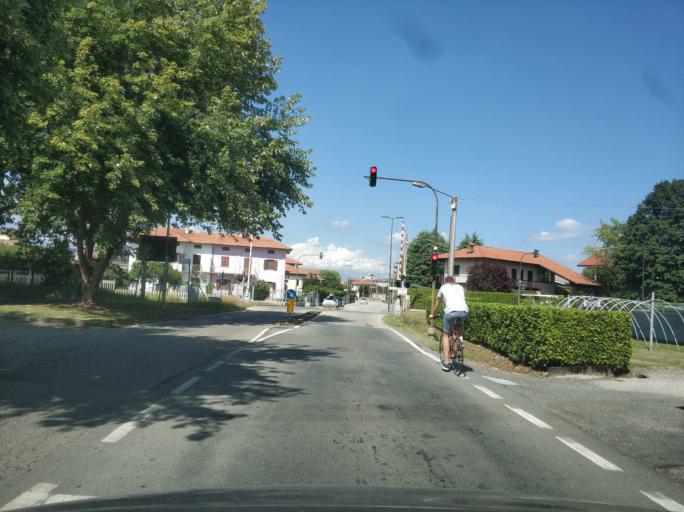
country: IT
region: Piedmont
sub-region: Provincia di Torino
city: Rivarolo Canavese
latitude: 45.3249
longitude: 7.7210
